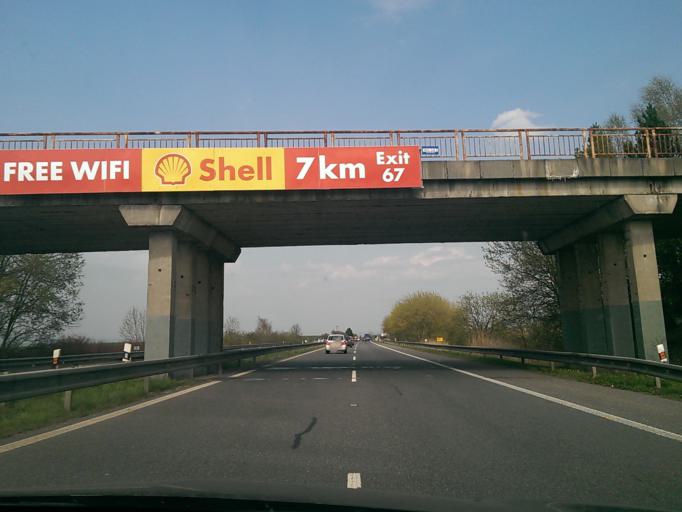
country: CZ
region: Central Bohemia
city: Mnichovo Hradiste
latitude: 50.5272
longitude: 15.0036
